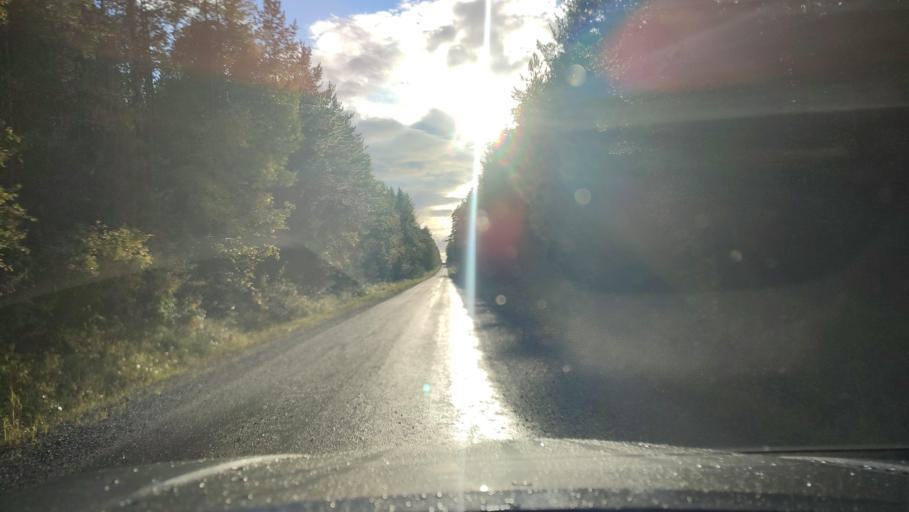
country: FI
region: Ostrobothnia
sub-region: Sydosterbotten
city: Kristinestad
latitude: 62.3046
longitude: 21.5248
